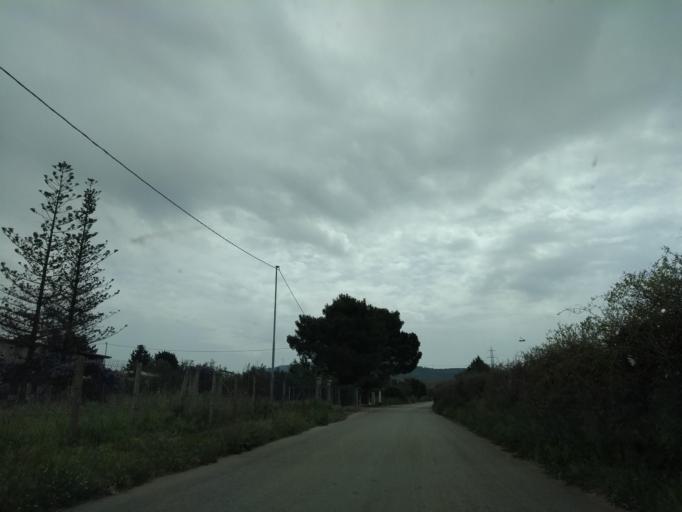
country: IT
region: Sicily
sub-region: Palermo
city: Partinico
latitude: 37.9965
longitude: 13.0655
